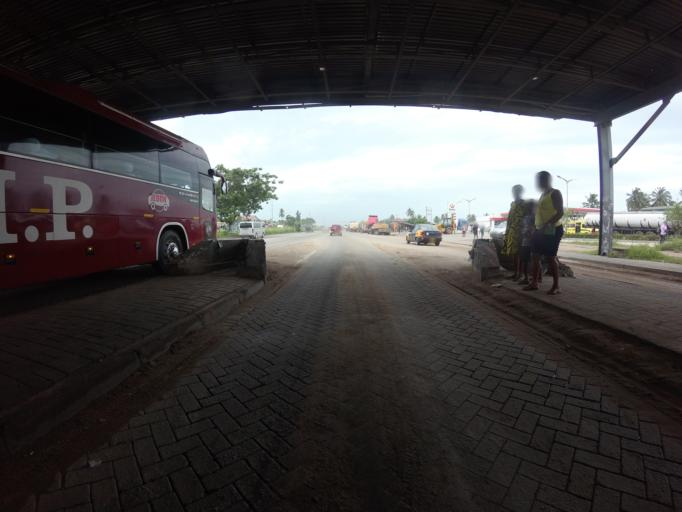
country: GH
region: Greater Accra
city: Achiaman
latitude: 5.7342
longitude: -0.3136
